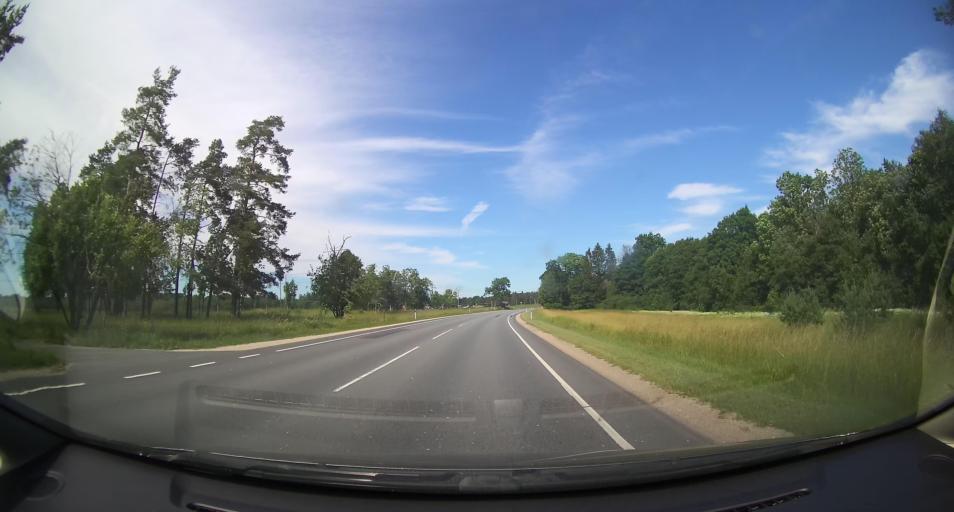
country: EE
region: Harju
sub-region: Nissi vald
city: Turba
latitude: 59.0238
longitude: 24.1480
